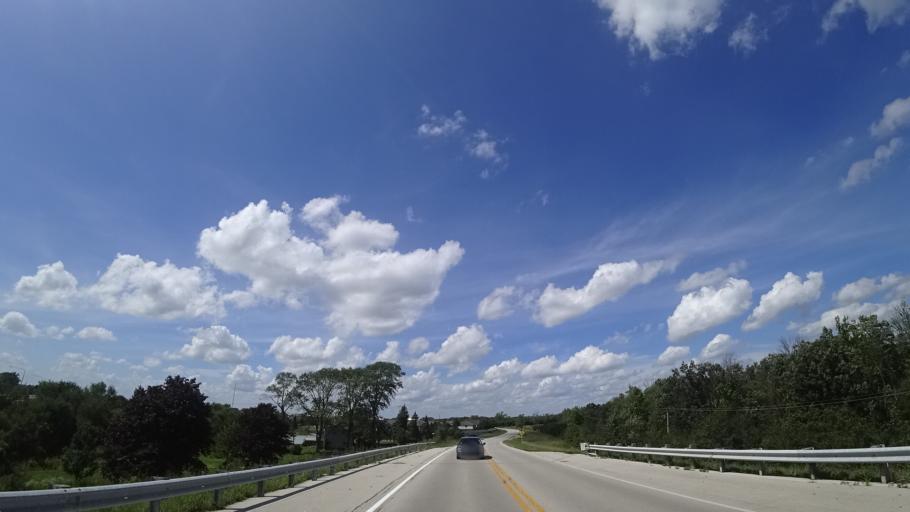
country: US
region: Illinois
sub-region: Cook County
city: Tinley Park
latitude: 41.5574
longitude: -87.7634
